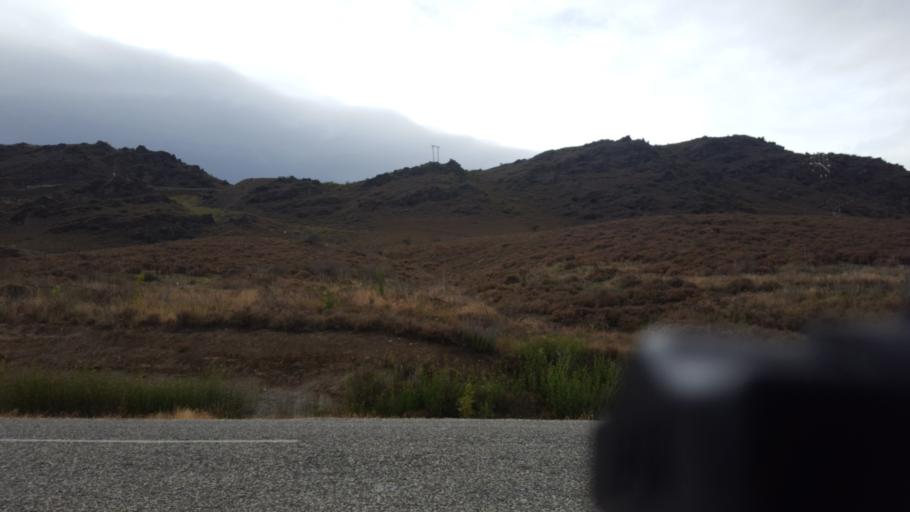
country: NZ
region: Otago
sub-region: Queenstown-Lakes District
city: Wanaka
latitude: -45.2534
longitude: 169.4026
